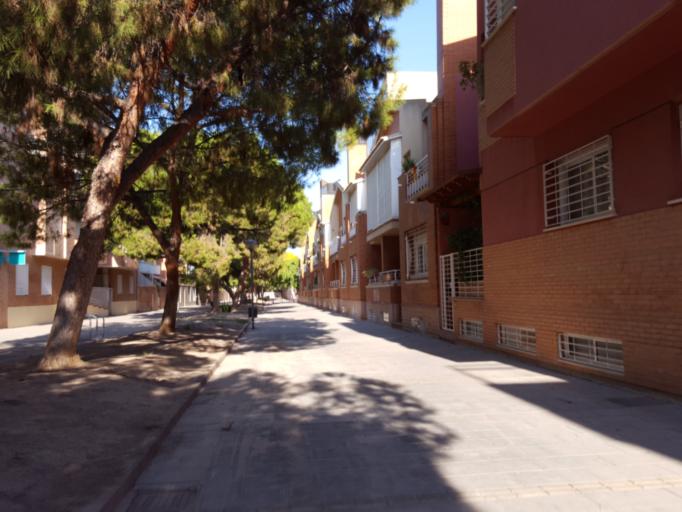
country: ES
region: Murcia
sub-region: Murcia
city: Murcia
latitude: 37.9950
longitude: -1.1226
